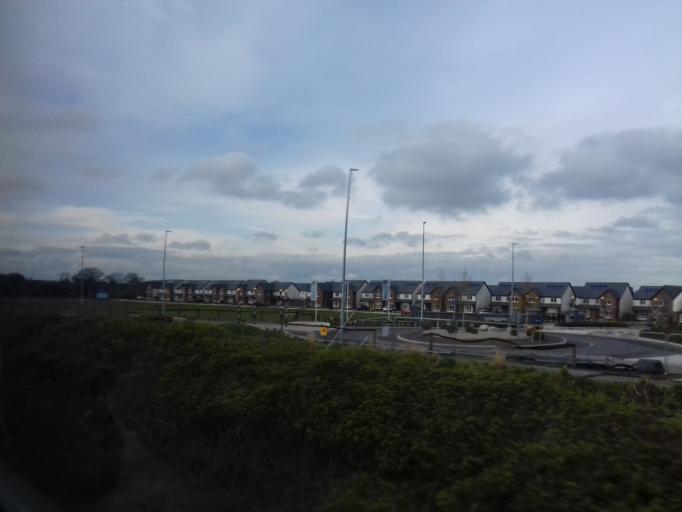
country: IE
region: Leinster
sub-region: Kildare
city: Kilcock
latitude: 53.3954
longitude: -6.6570
